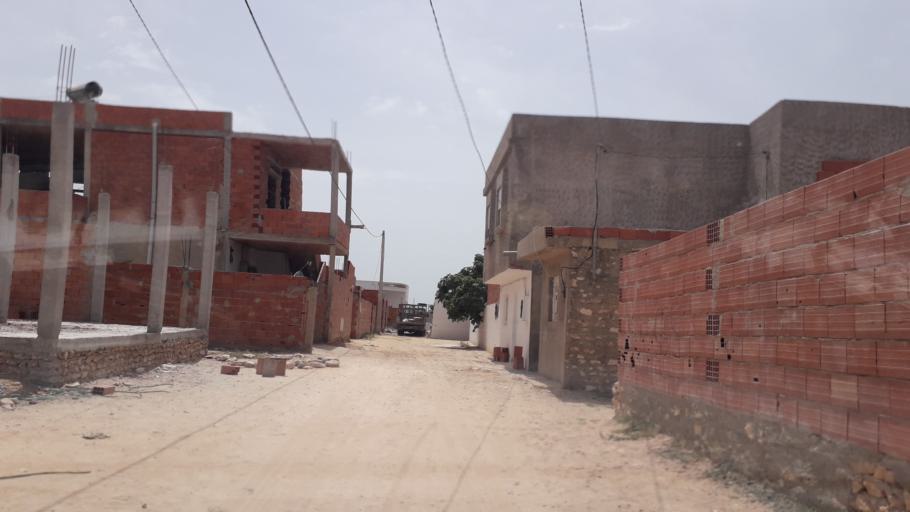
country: TN
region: Safaqis
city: Al Qarmadah
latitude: 34.8402
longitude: 10.7773
